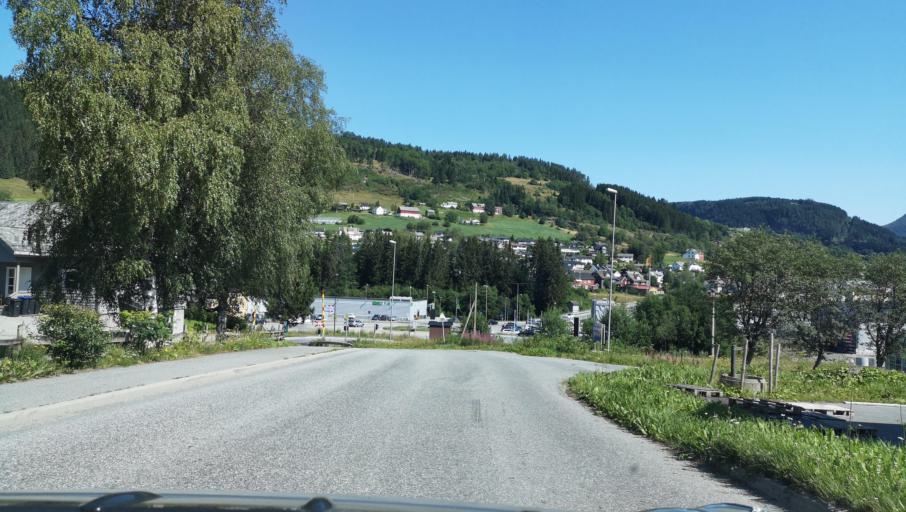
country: NO
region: Hordaland
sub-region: Voss
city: Voss
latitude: 60.6346
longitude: 6.4644
